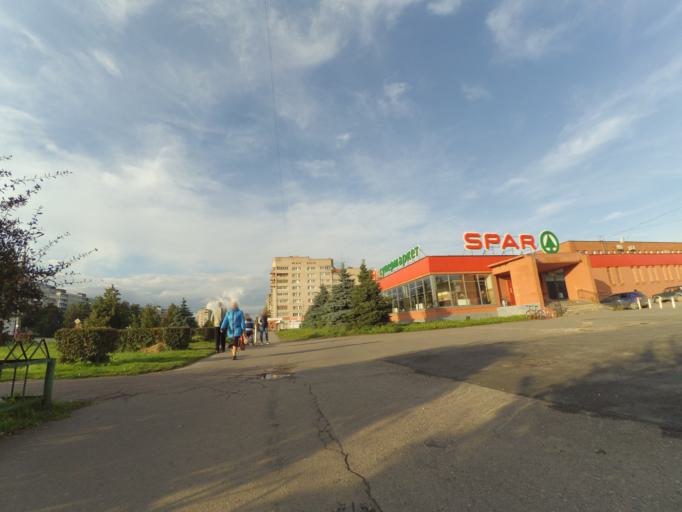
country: RU
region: Novgorod
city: Velikiy Novgorod
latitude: 58.5307
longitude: 31.2329
